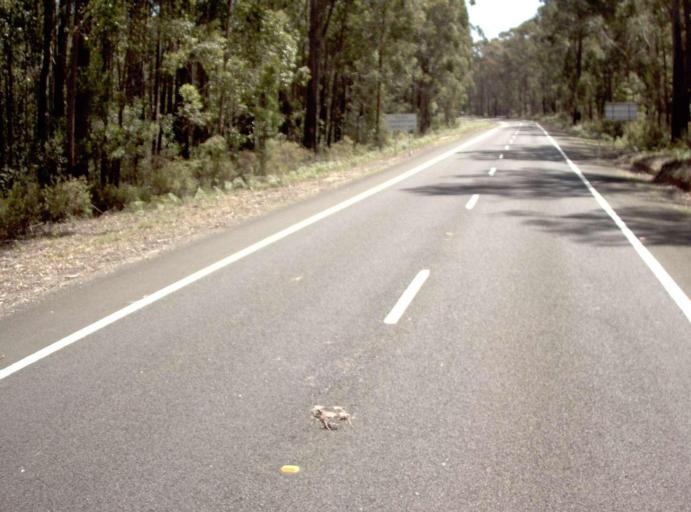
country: AU
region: New South Wales
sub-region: Bombala
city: Bombala
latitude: -37.5656
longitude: 149.0405
